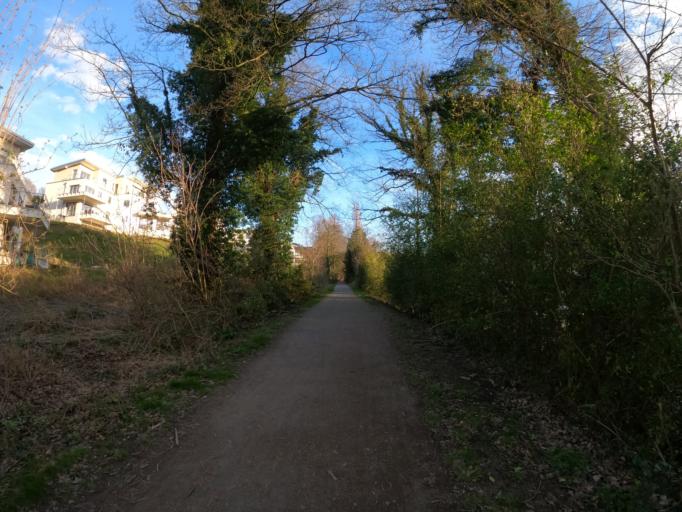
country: DE
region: North Rhine-Westphalia
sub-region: Regierungsbezirk Dusseldorf
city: Wuppertal
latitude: 51.2441
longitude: 7.1123
